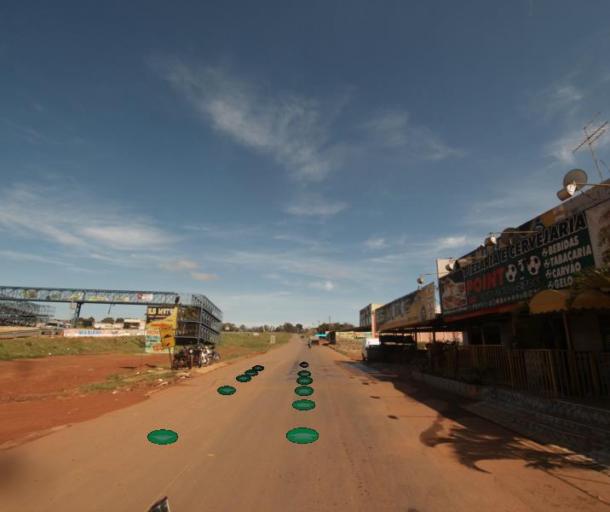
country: BR
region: Federal District
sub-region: Brasilia
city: Brasilia
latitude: -15.7597
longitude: -48.2453
